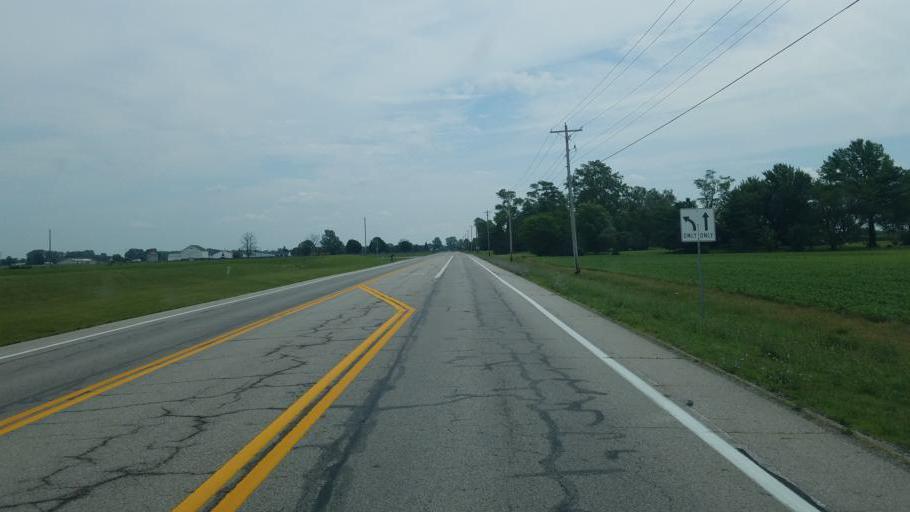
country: US
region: Ohio
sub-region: Franklin County
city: Hilliard
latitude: 40.0360
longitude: -83.2160
